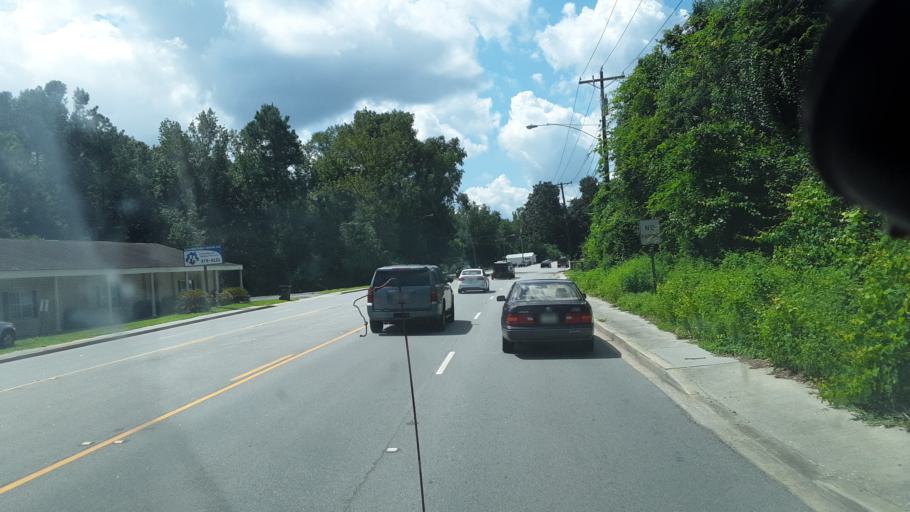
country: US
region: South Carolina
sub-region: Berkeley County
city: Moncks Corner
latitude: 33.1899
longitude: -80.0171
